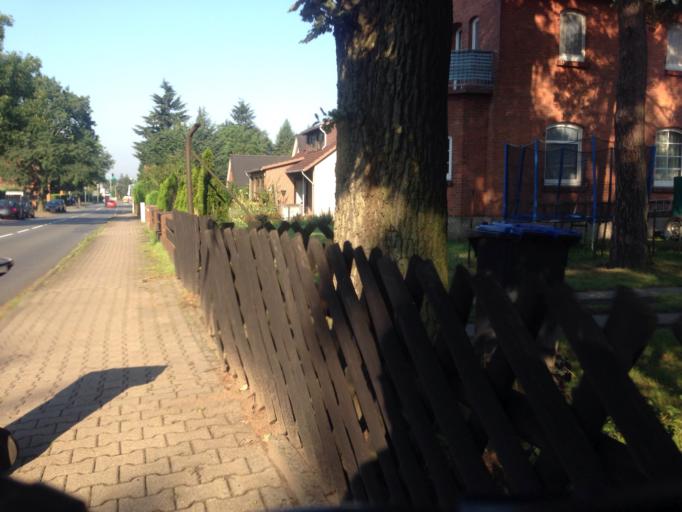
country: DE
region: Lower Saxony
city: Adendorf
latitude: 53.2726
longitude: 10.4306
